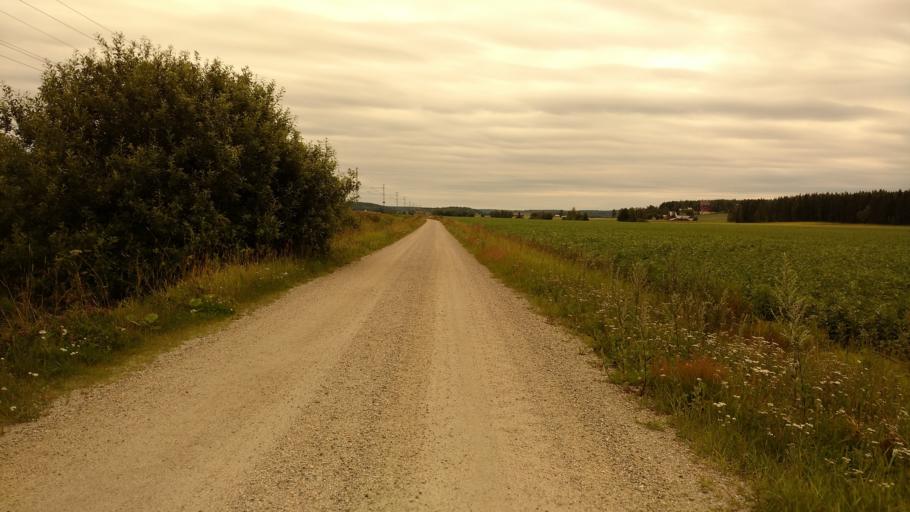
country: FI
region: Varsinais-Suomi
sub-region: Turku
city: Paimio
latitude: 60.4230
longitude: 22.8158
